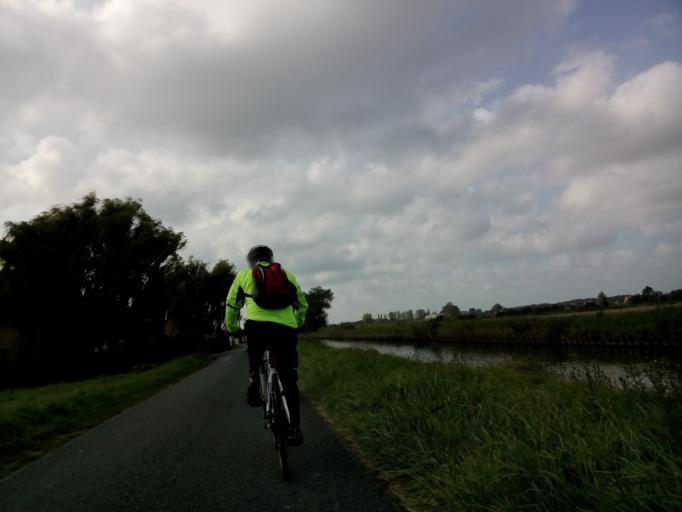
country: FR
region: Nord-Pas-de-Calais
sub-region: Departement du Pas-de-Calais
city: Les Attaques
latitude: 50.9002
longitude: 1.9513
